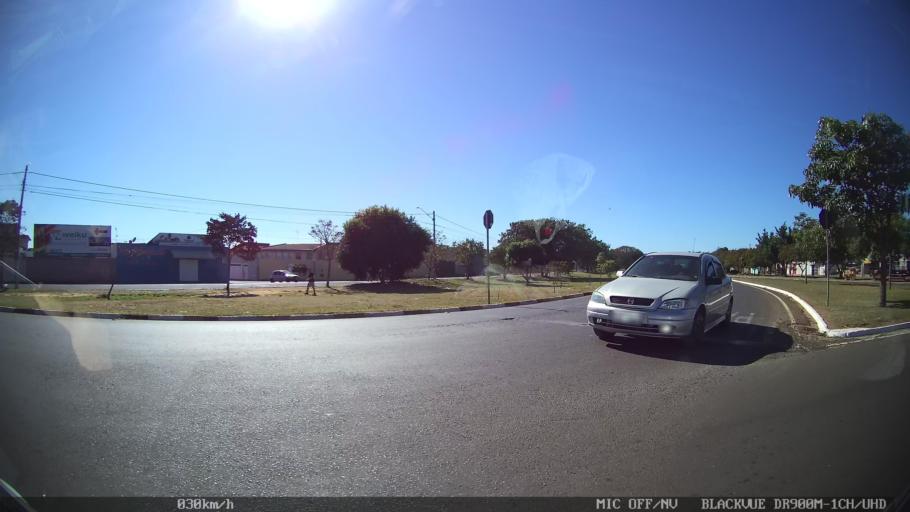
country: BR
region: Sao Paulo
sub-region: Franca
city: Franca
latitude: -20.5401
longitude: -47.3594
